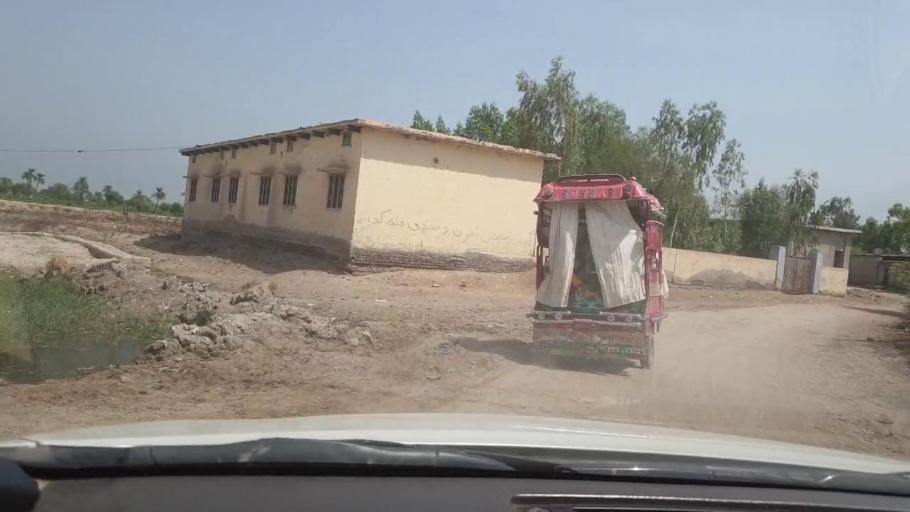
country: PK
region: Sindh
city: Shikarpur
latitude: 27.9339
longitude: 68.6022
